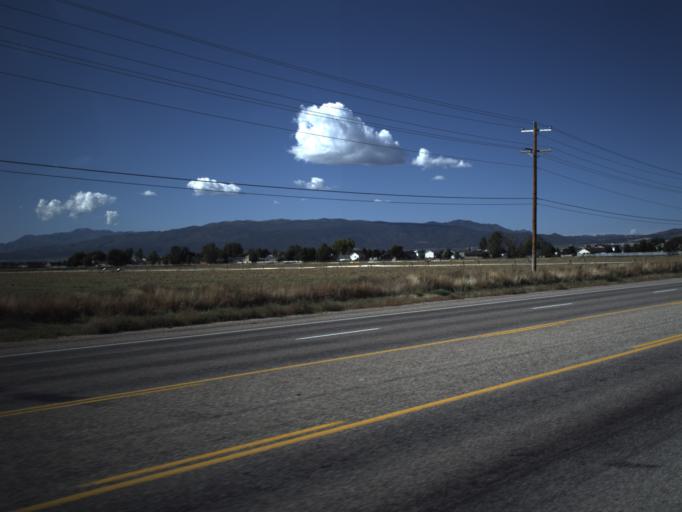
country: US
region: Utah
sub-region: Iron County
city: Cedar City
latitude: 37.6851
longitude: -113.1248
